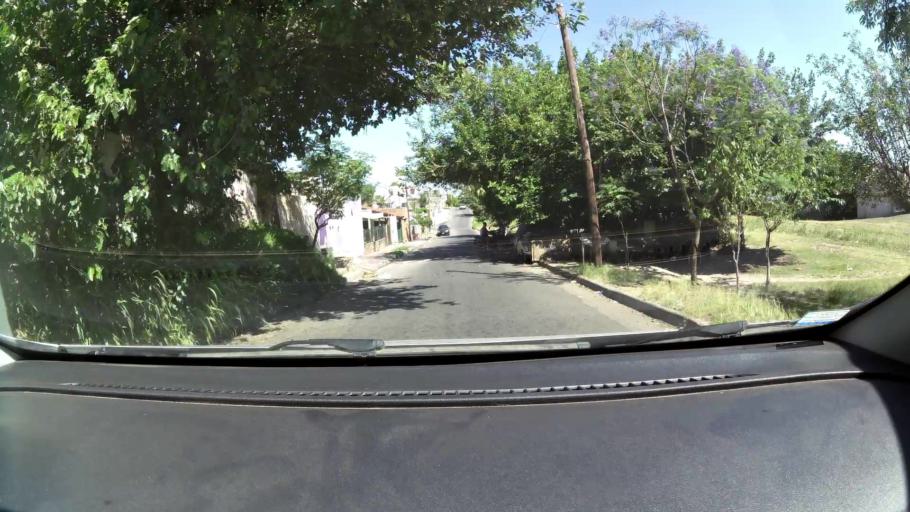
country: AR
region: Cordoba
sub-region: Departamento de Capital
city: Cordoba
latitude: -31.4289
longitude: -64.1527
